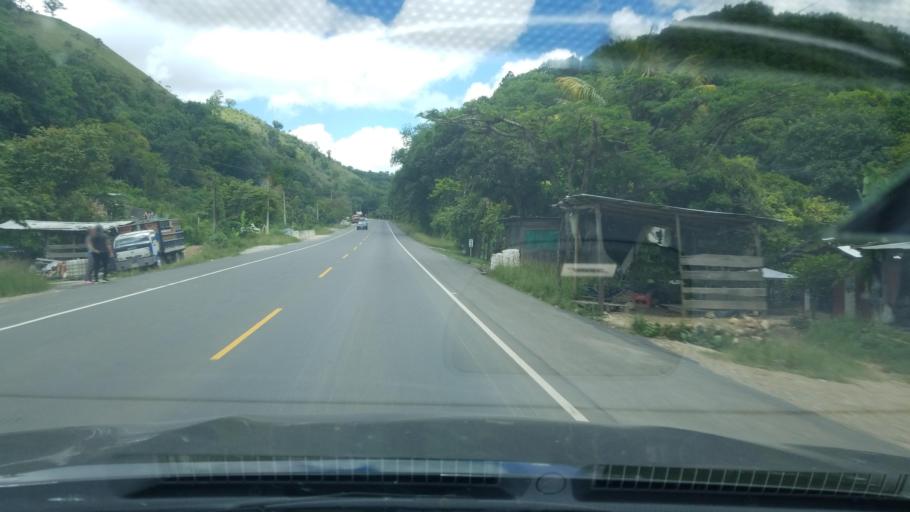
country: HN
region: Francisco Morazan
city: Talanga
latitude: 14.3754
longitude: -87.1370
